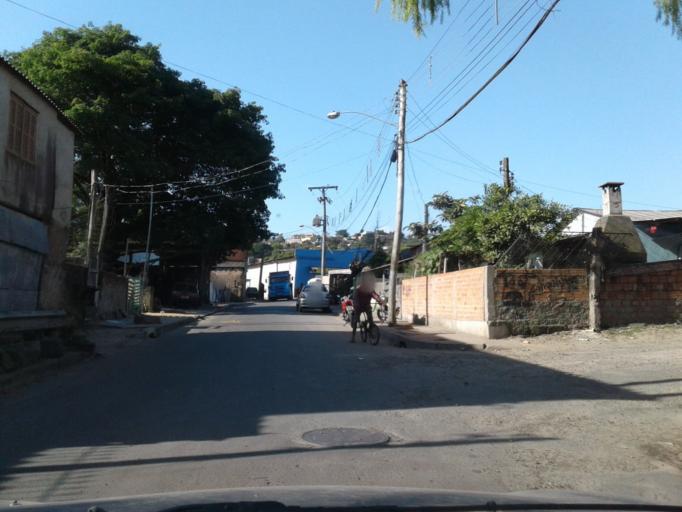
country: BR
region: Rio Grande do Sul
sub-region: Porto Alegre
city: Porto Alegre
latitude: -30.0502
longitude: -51.1584
